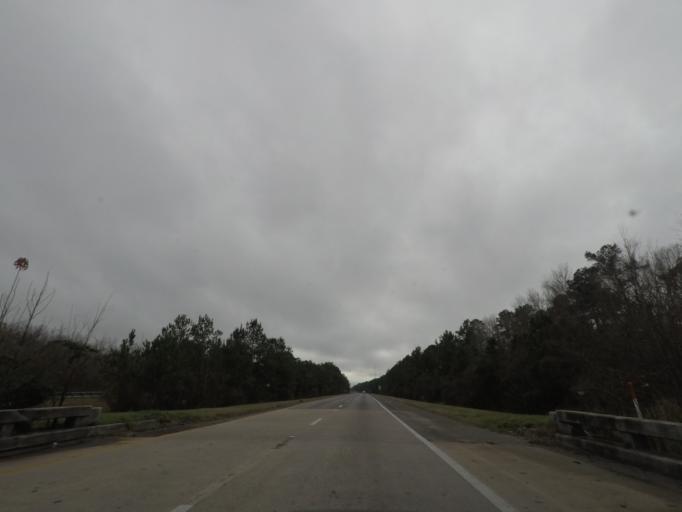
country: US
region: South Carolina
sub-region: Orangeburg County
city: Holly Hill
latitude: 33.3726
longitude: -80.5230
